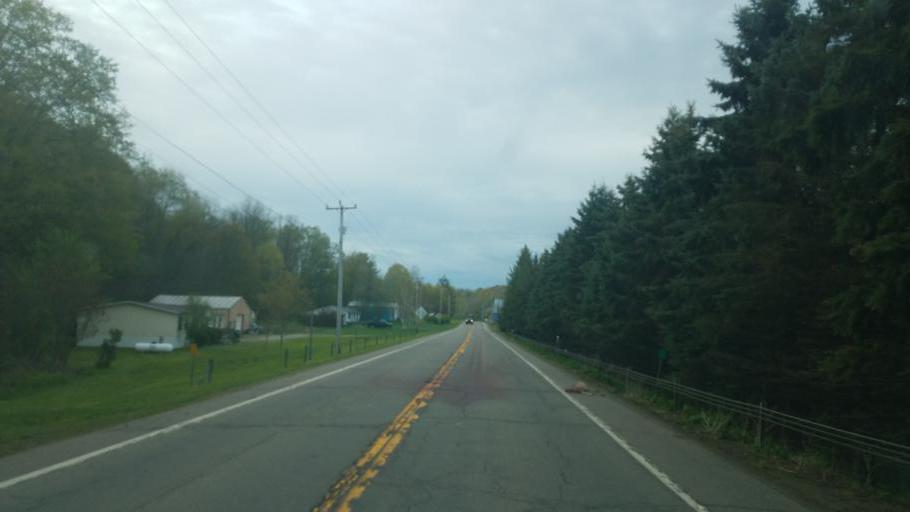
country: US
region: New York
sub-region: Steuben County
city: Canisteo
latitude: 42.2170
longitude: -77.5707
